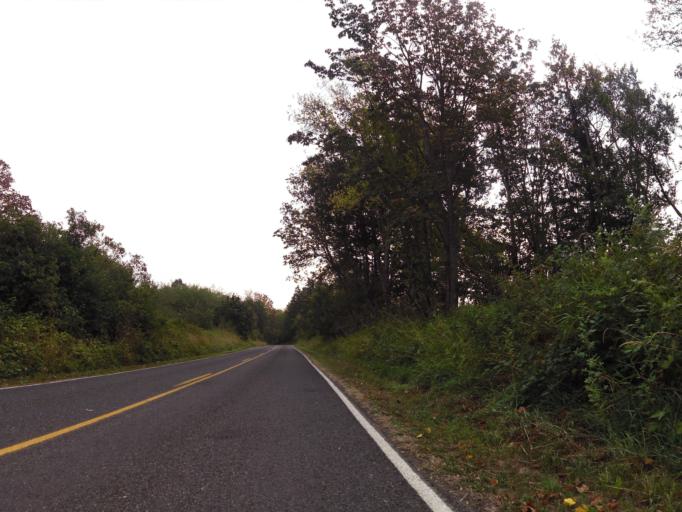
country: US
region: Washington
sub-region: Whatcom County
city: Ferndale
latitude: 48.8067
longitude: -122.6694
